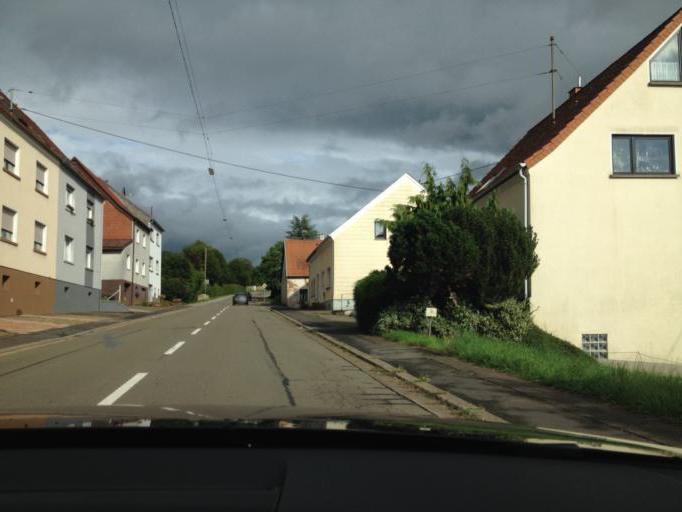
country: DE
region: Saarland
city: Oberthal
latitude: 49.5216
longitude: 7.1092
